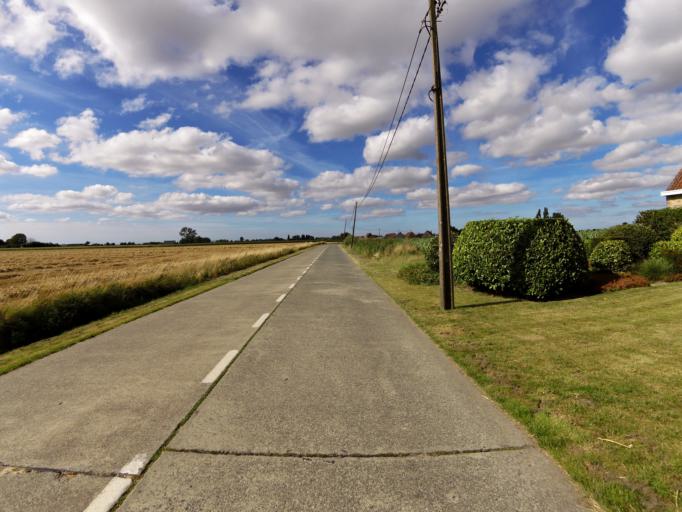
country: BE
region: Flanders
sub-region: Provincie West-Vlaanderen
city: Alveringem
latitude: 50.9772
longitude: 2.6608
